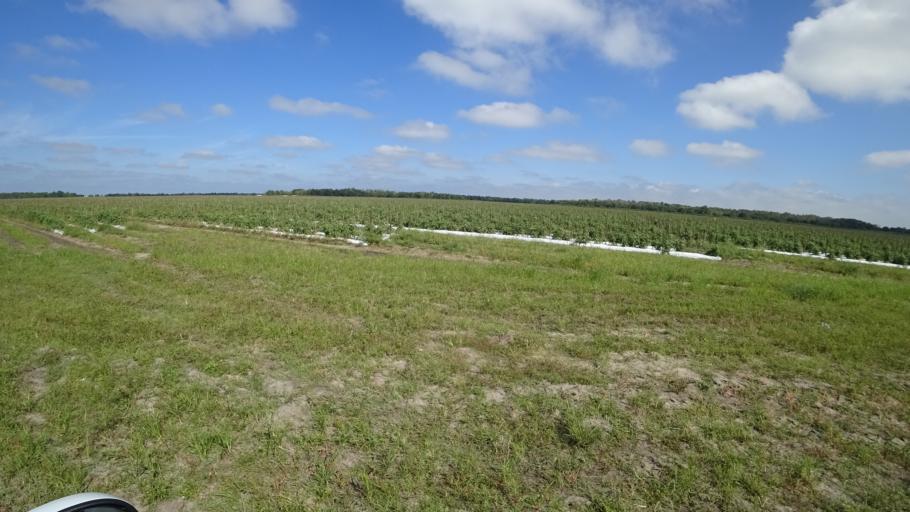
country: US
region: Florida
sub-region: DeSoto County
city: Arcadia
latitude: 27.2811
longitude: -82.0828
